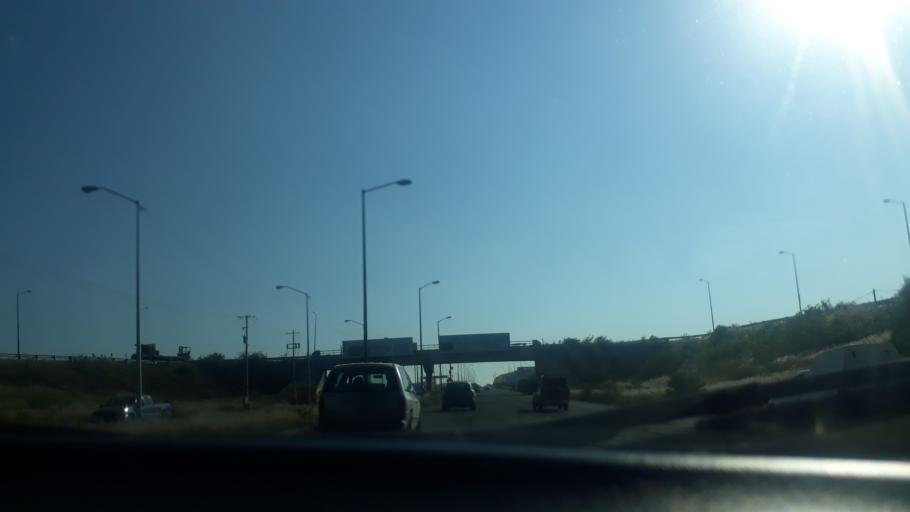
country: MX
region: Puebla
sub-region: Puebla
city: Articulo Primero Constitucional
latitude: 18.9865
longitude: -98.1688
